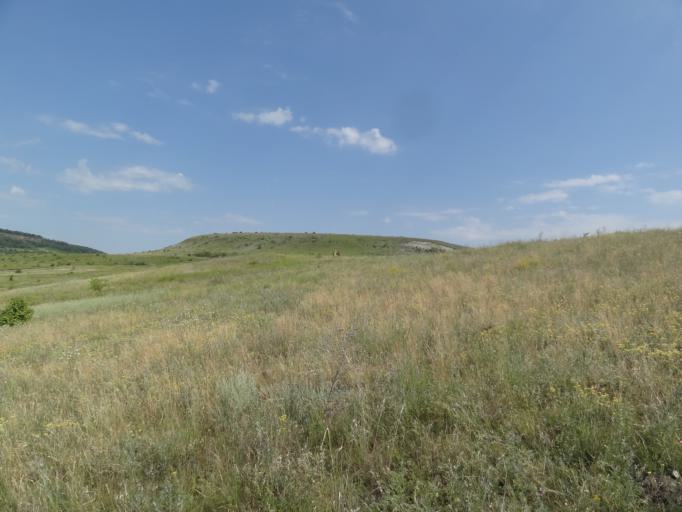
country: RU
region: Saratov
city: Krasnyy Oktyabr'
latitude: 51.4291
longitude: 45.7943
